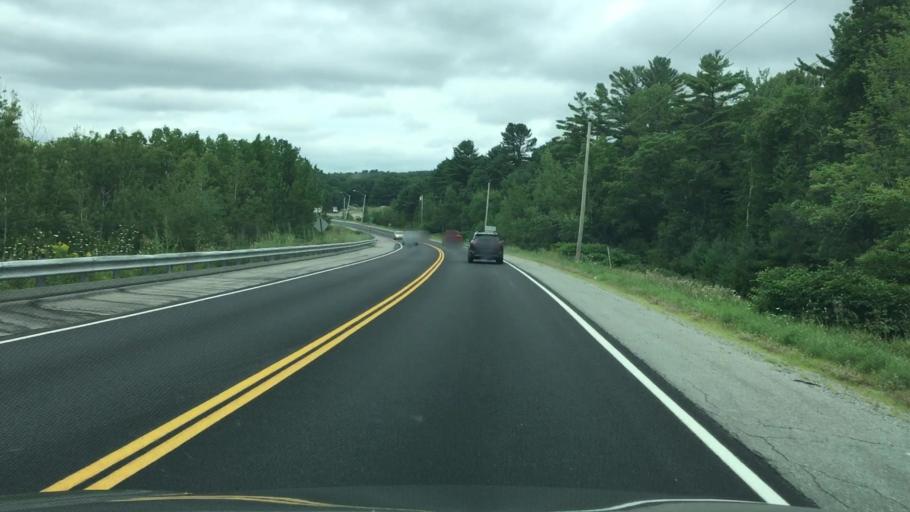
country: US
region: Maine
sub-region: Penobscot County
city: Orrington
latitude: 44.6913
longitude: -68.8111
